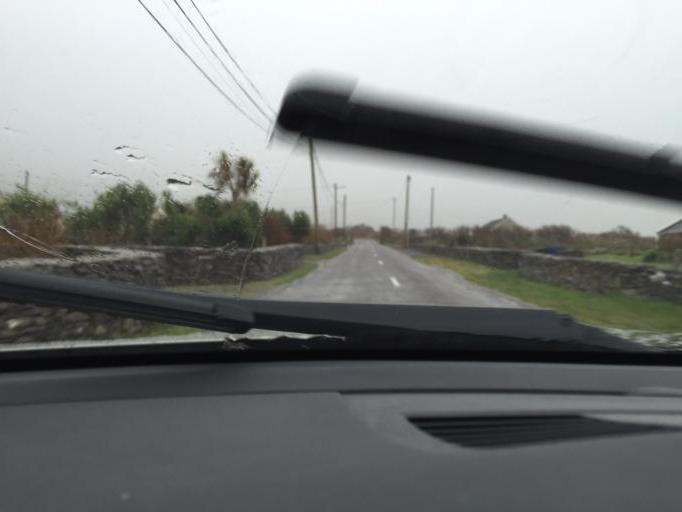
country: IE
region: Munster
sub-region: Ciarrai
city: Dingle
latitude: 52.1336
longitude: -10.4513
